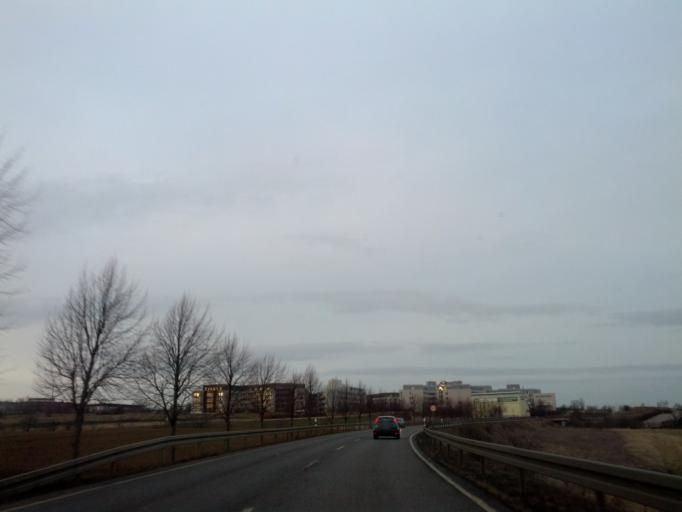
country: DE
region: Thuringia
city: Ingersleben
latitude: 50.9682
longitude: 10.9562
